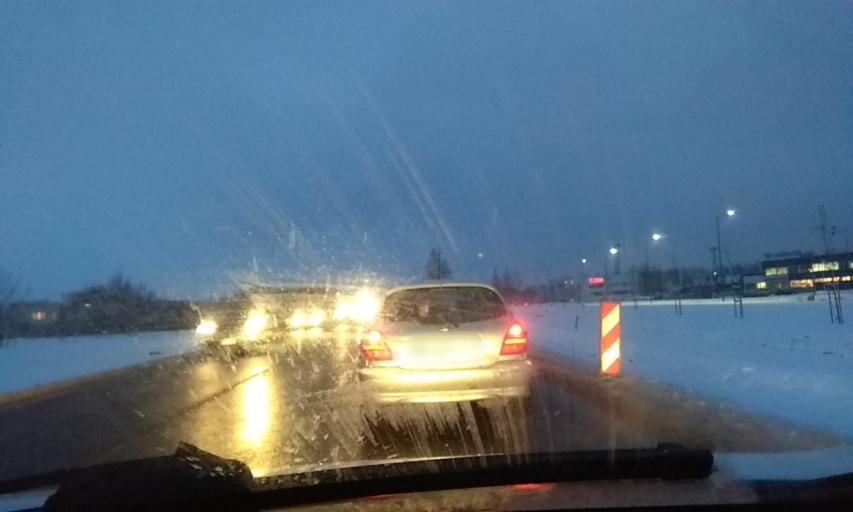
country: LT
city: Ramuciai
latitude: 54.9059
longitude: 24.0294
